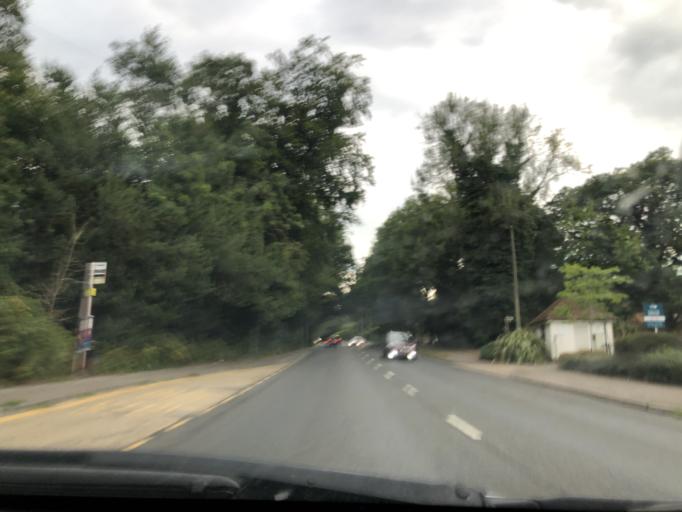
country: GB
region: England
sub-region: Kent
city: Sevenoaks
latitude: 51.2550
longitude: 0.1991
